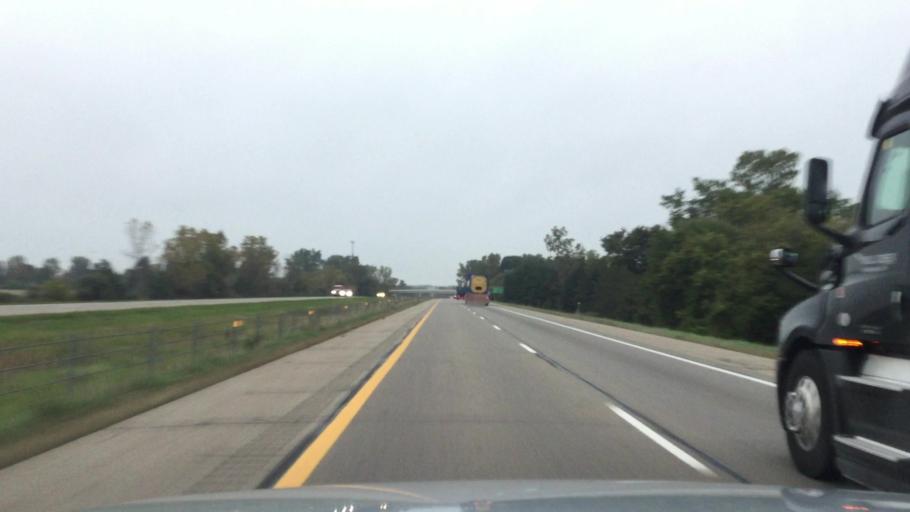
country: US
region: Michigan
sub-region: Shiawassee County
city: Durand
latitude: 42.9396
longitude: -83.9844
